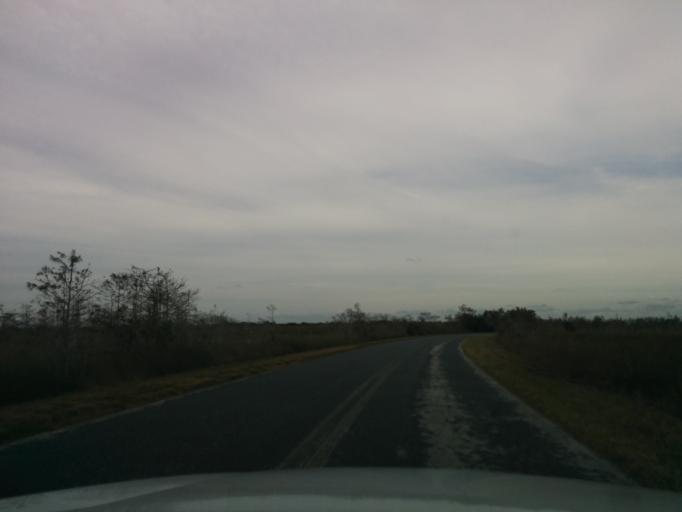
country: US
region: Florida
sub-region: Miami-Dade County
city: Florida City
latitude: 25.4345
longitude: -80.7807
